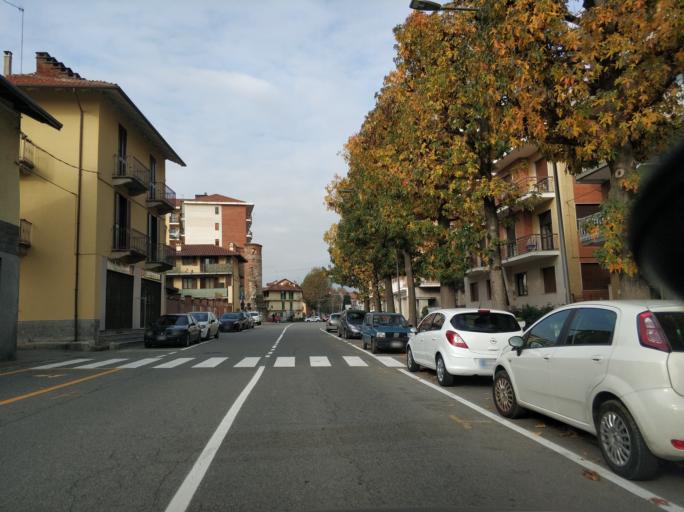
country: IT
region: Piedmont
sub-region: Provincia di Torino
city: San Carlo Canavese
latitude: 45.2370
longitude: 7.6047
